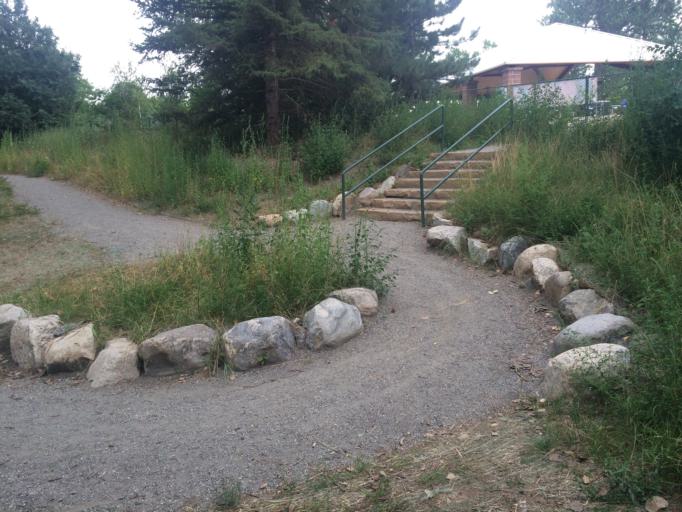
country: US
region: Colorado
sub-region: Jefferson County
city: Wheat Ridge
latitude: 39.7743
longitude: -105.0988
